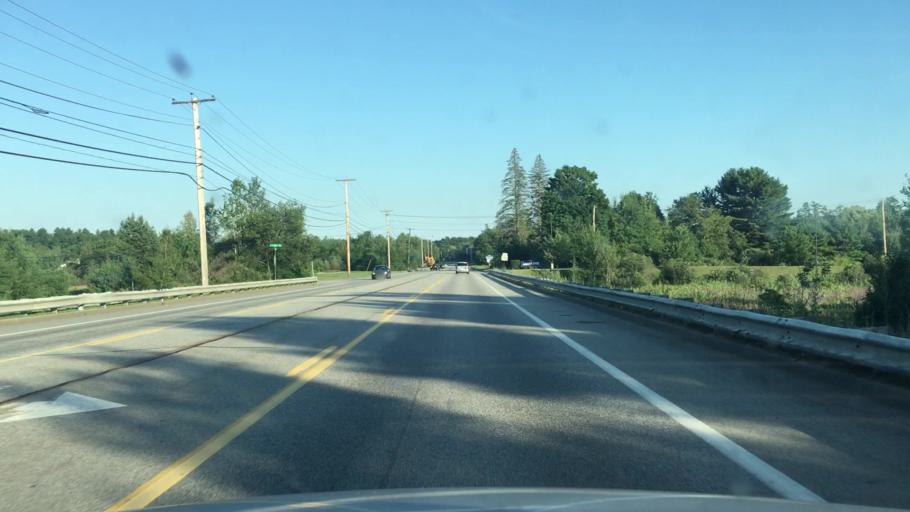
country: US
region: Maine
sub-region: Androscoggin County
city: Lisbon
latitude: 44.0575
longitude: -70.1429
